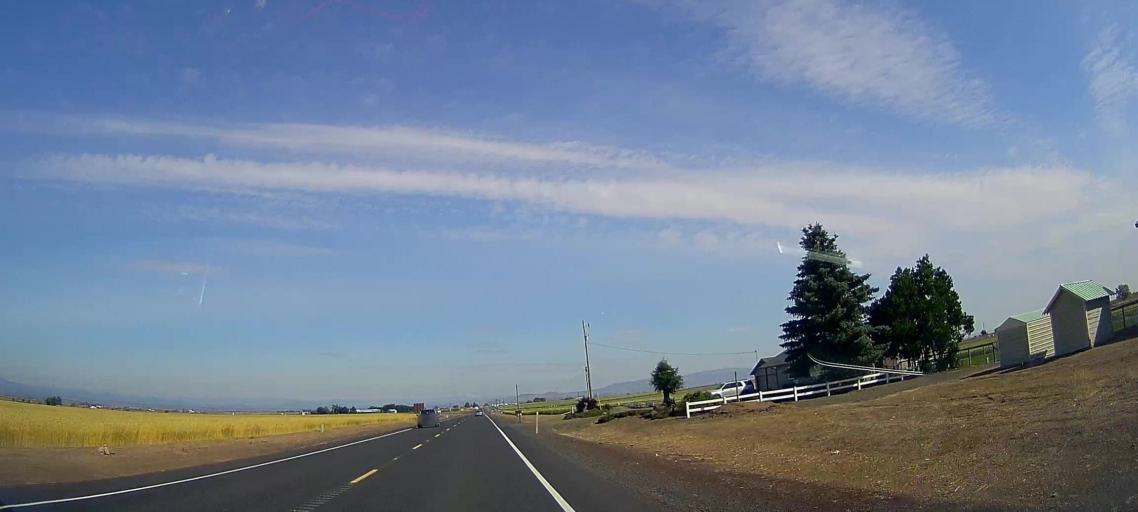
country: US
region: Oregon
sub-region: Jefferson County
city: Madras
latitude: 44.6751
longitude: -121.1433
